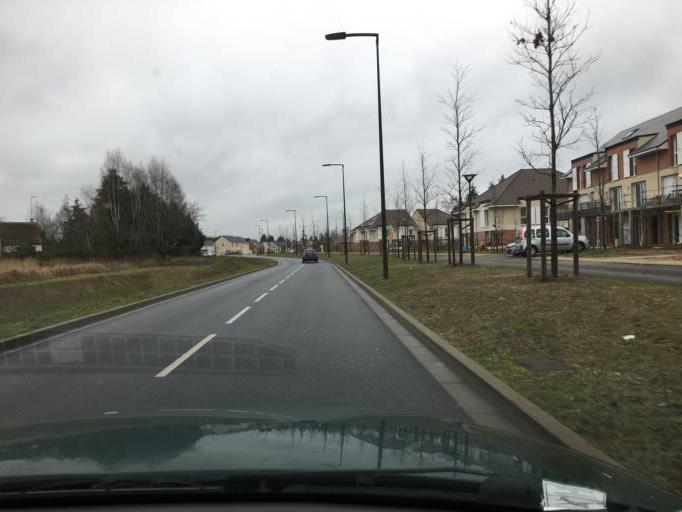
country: FR
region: Centre
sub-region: Departement du Loiret
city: Saint-Pryve-Saint-Mesmin
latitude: 47.8616
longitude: 1.8773
